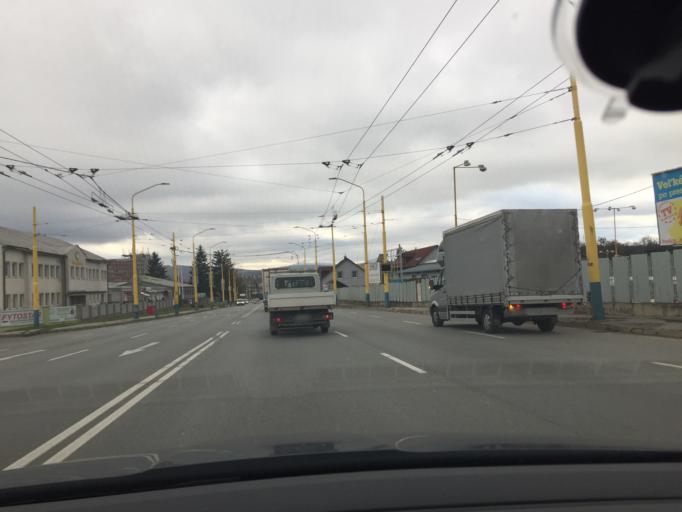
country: SK
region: Presovsky
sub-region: Okres Presov
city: Presov
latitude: 49.0127
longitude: 21.2627
